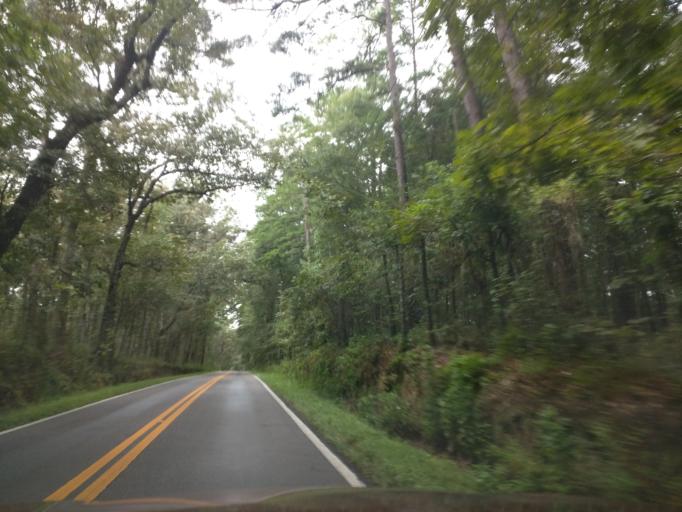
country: US
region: Florida
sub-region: Leon County
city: Tallahassee
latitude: 30.5095
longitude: -84.1463
